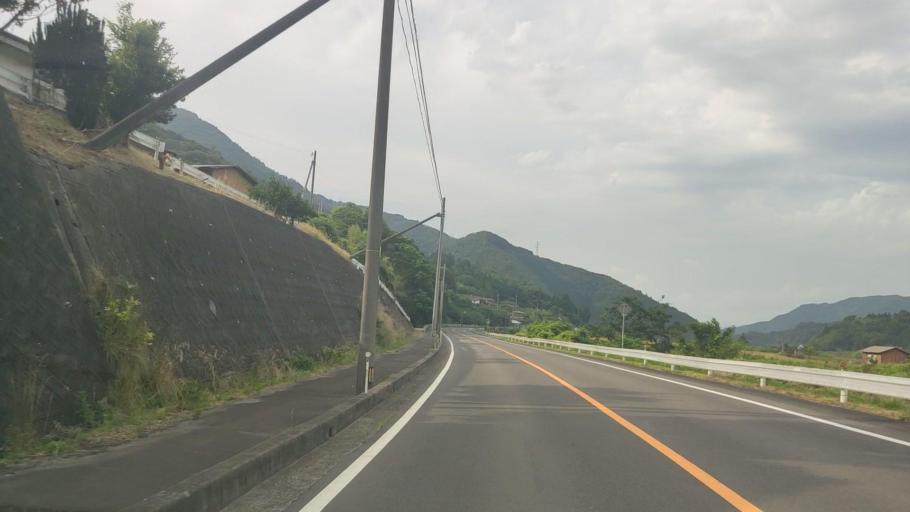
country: JP
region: Tottori
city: Kurayoshi
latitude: 35.3428
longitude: 133.8411
